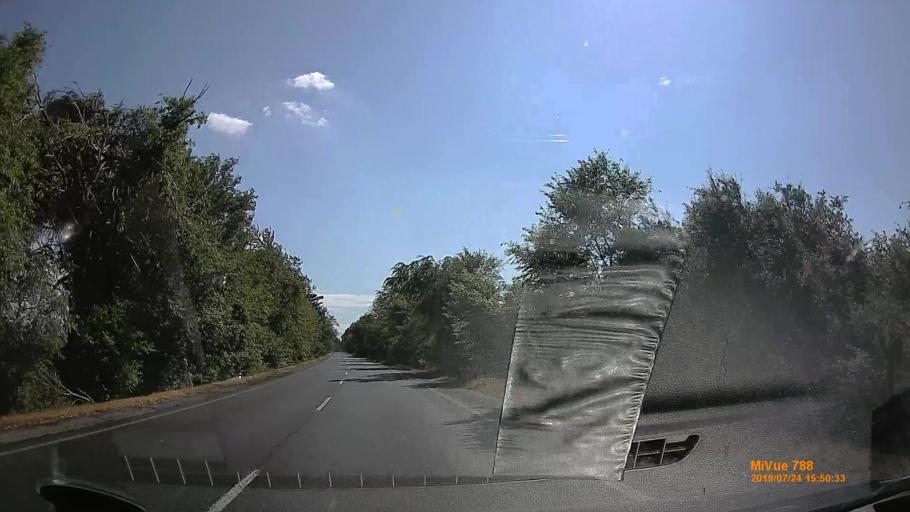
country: HU
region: Szabolcs-Szatmar-Bereg
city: Nyirmada
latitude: 48.0498
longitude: 22.1958
